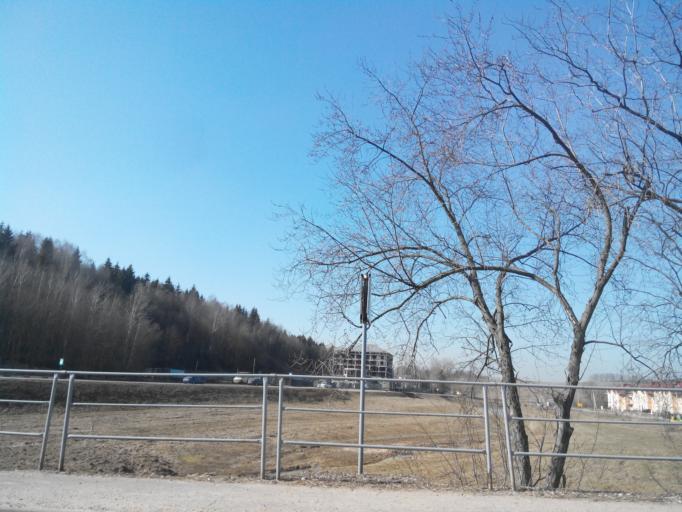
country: BY
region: Minsk
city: Zhdanovichy
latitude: 53.9150
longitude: 27.3906
